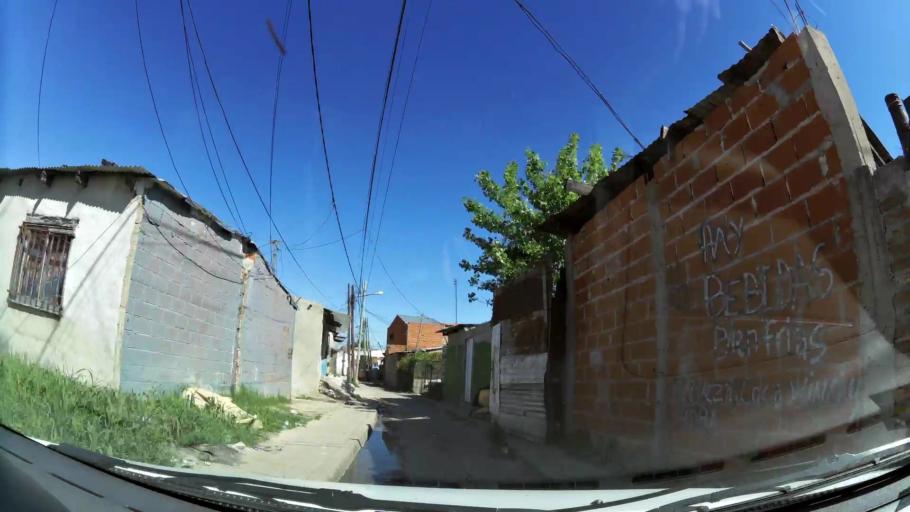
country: AR
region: Buenos Aires
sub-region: Partido de Tigre
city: Tigre
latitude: -34.5095
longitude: -58.5852
